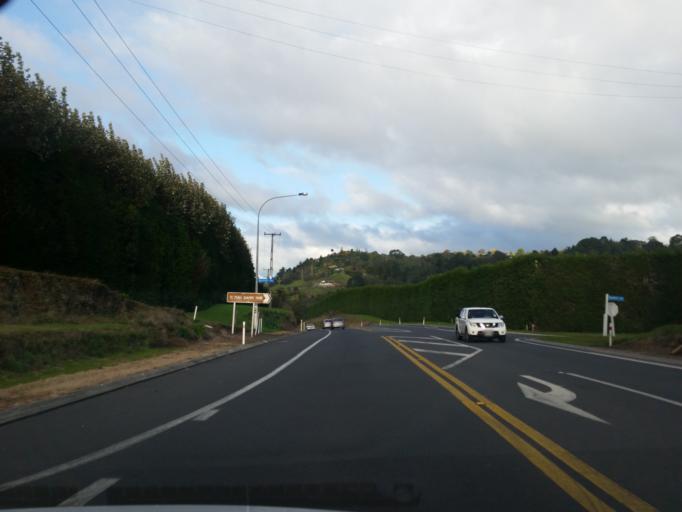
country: NZ
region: Bay of Plenty
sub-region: Tauranga City
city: Tauranga
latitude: -37.6952
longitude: 176.0497
